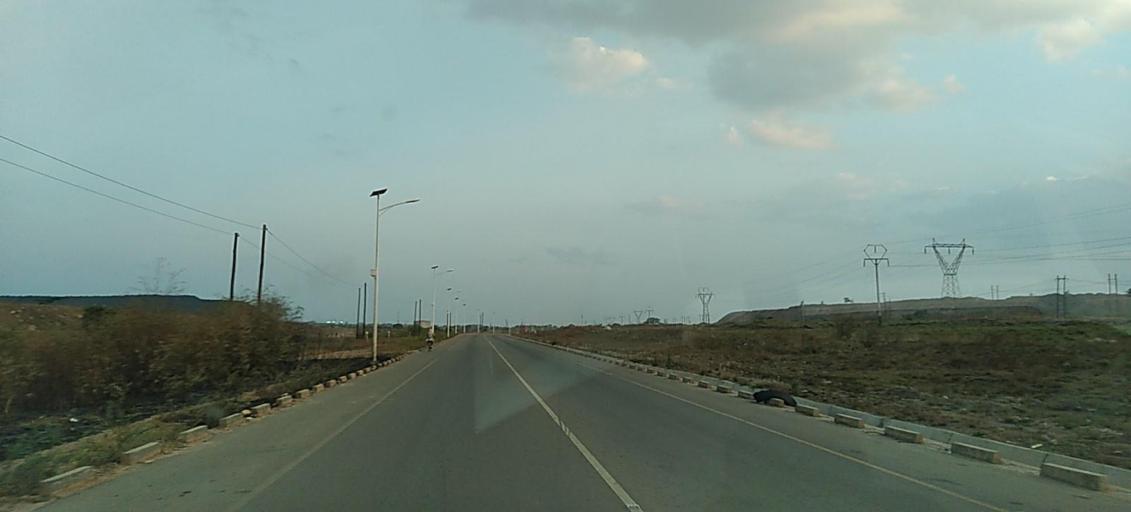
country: ZM
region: Copperbelt
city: Chingola
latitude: -12.5269
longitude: 27.8334
